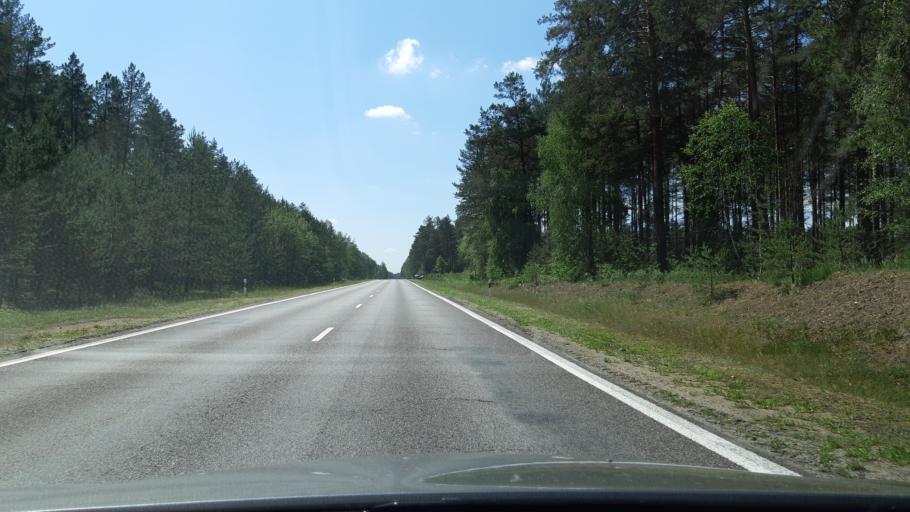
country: LT
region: Alytaus apskritis
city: Druskininkai
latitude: 54.0909
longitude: 24.1979
